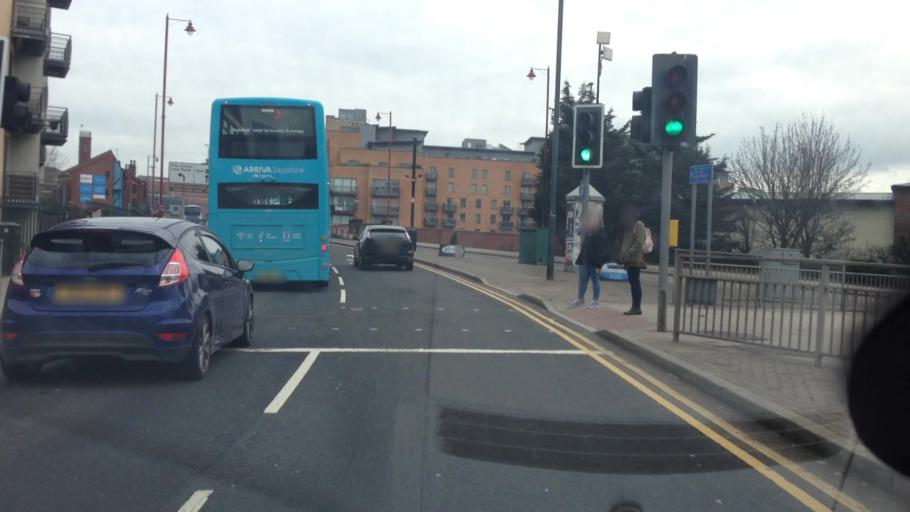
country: GB
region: England
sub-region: City and Borough of Leeds
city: Leeds
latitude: 53.7927
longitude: -1.5359
